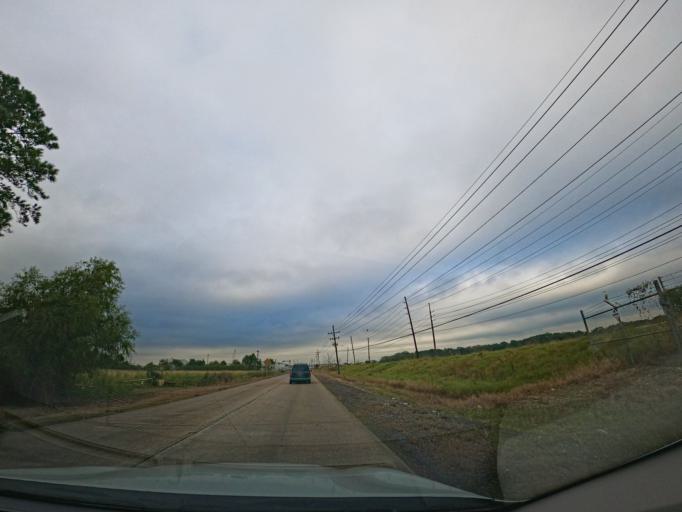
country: US
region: Louisiana
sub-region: Terrebonne Parish
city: Houma
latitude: 29.5732
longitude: -90.7020
